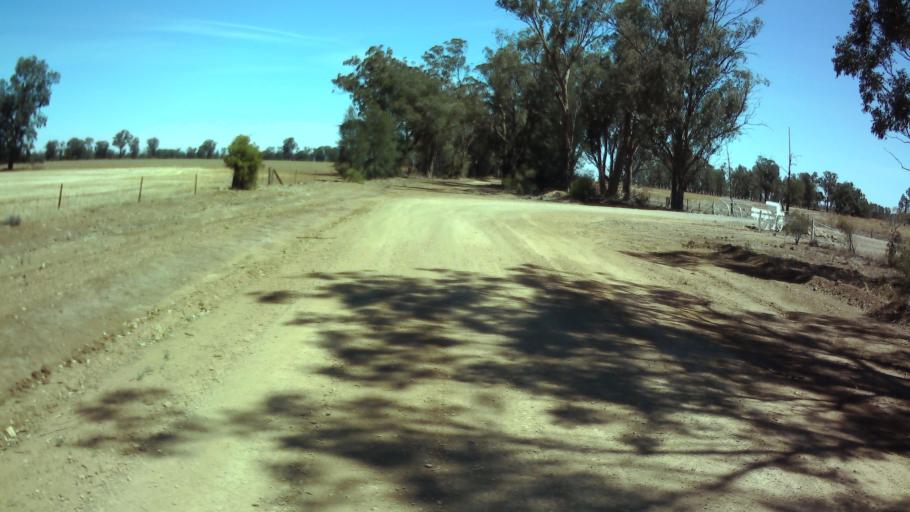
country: AU
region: New South Wales
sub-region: Bland
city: West Wyalong
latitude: -33.9129
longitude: 147.6842
